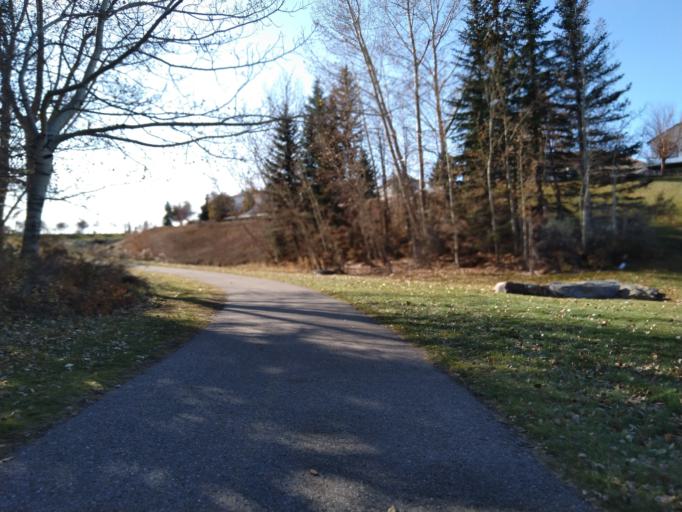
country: CA
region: Alberta
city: Calgary
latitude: 51.1485
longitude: -114.1132
